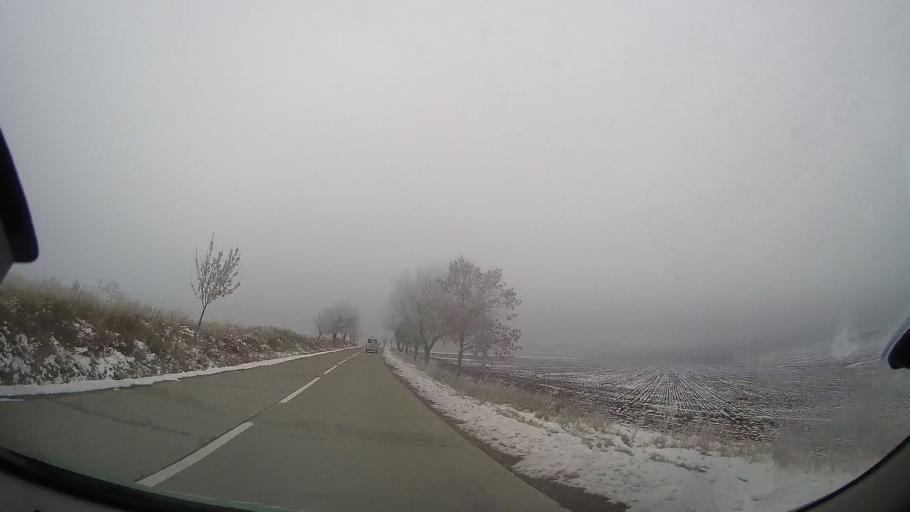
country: RO
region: Vaslui
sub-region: Comuna Ivesti
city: Ivesti
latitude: 46.1970
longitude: 27.5953
